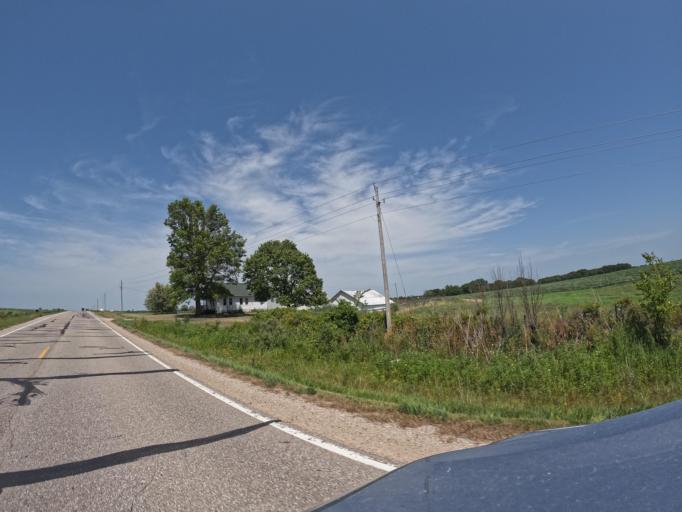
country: US
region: Iowa
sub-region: Henry County
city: Mount Pleasant
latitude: 40.9899
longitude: -91.6123
